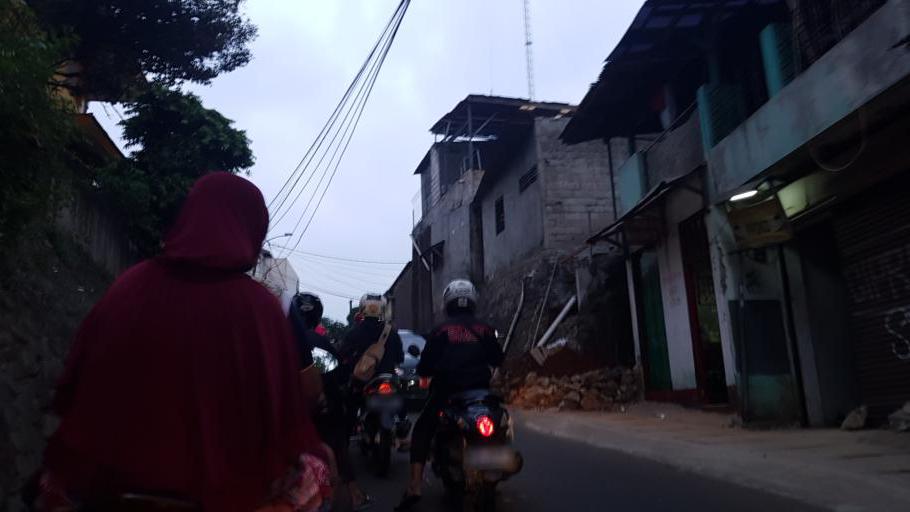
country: ID
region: West Java
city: Depok
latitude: -6.3631
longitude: 106.8013
